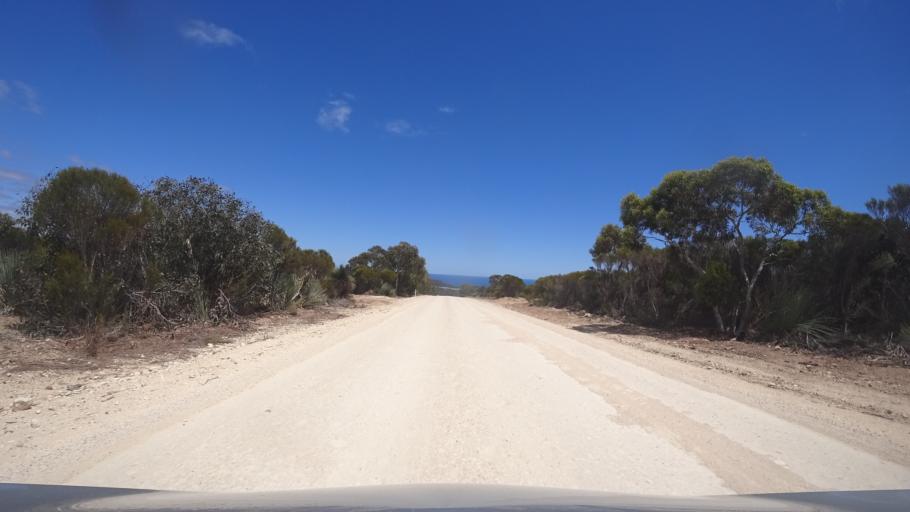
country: AU
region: South Australia
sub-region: Kangaroo Island
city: Kingscote
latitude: -35.6378
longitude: 137.2251
